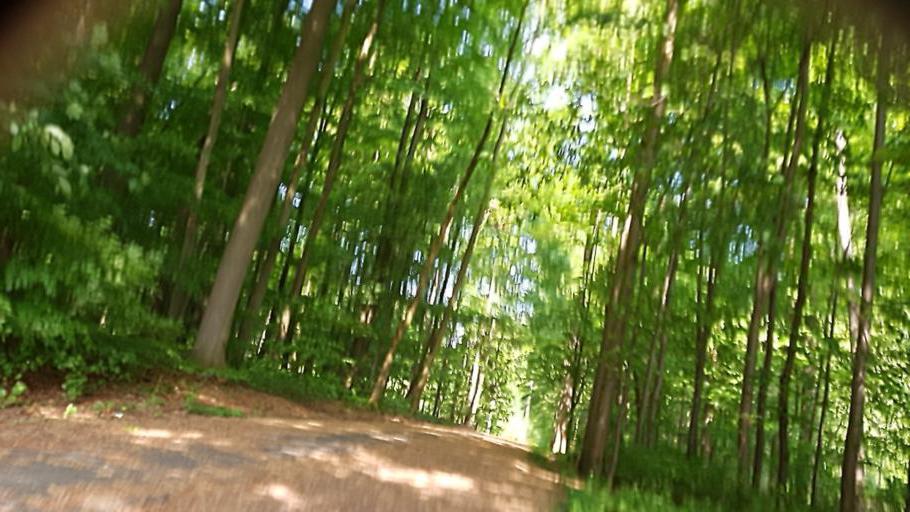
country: BE
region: Flanders
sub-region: Provincie Vlaams-Brabant
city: Tervuren
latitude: 50.8082
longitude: 4.5328
